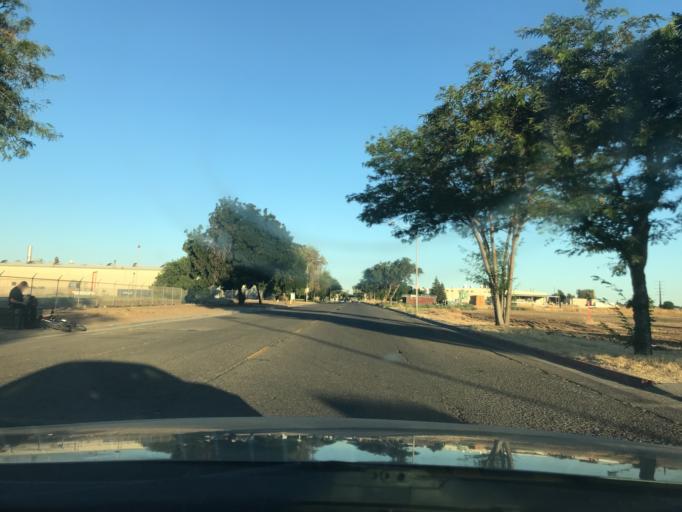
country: US
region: California
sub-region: Merced County
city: Merced
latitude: 37.3164
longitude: -120.5112
